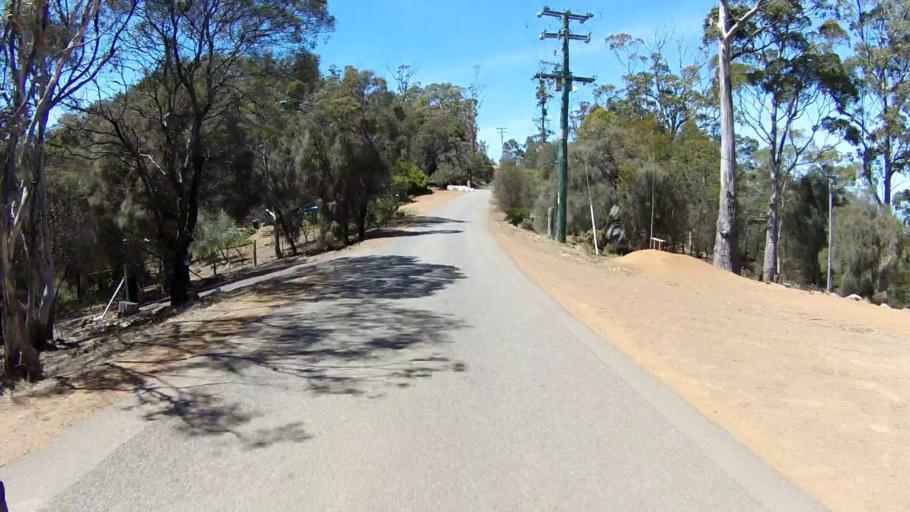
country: AU
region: Tasmania
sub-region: Clarence
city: Cambridge
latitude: -42.8597
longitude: 147.4501
